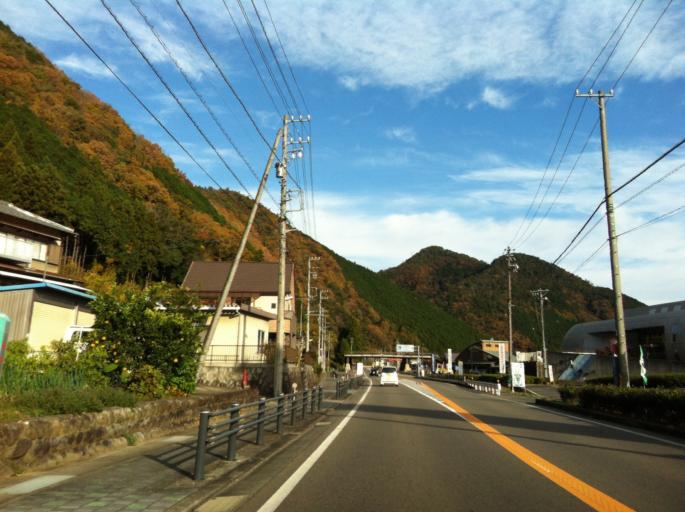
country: JP
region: Gifu
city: Minokamo
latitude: 35.5322
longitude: 137.1144
